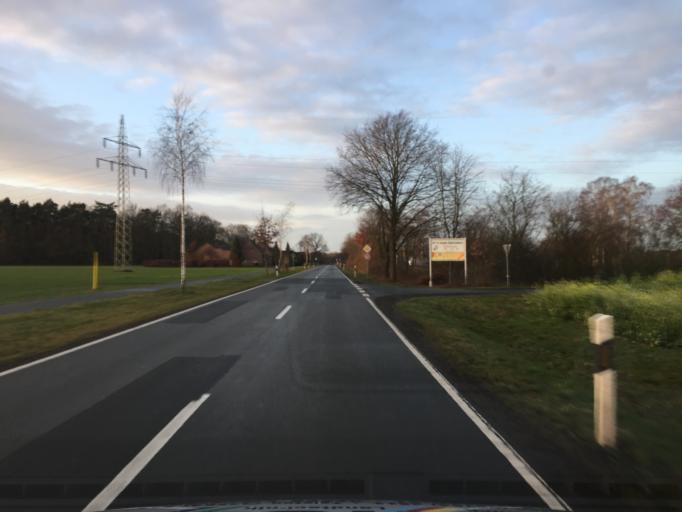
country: DE
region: Lower Saxony
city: Raddestorf
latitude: 52.4463
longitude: 8.9411
